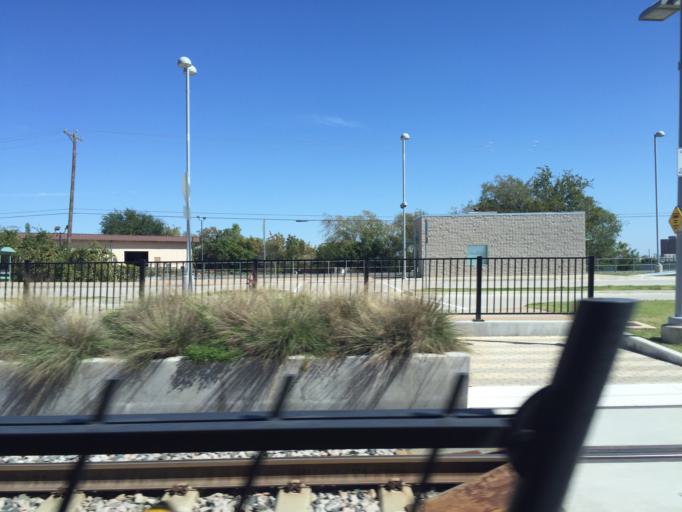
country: US
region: Texas
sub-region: Dallas County
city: Coppell
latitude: 32.8877
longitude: -96.9860
